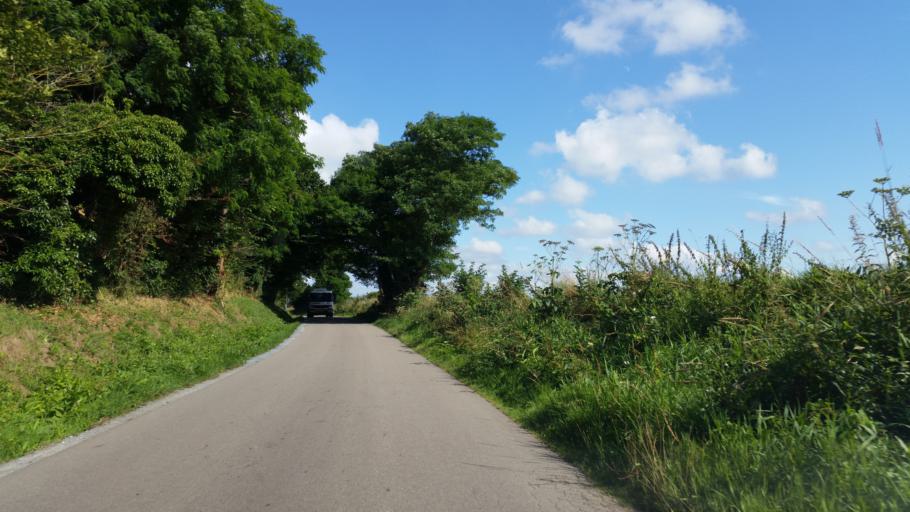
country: FR
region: Lower Normandy
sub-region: Departement du Calvados
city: Amfreville
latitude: 49.2482
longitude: -0.2258
